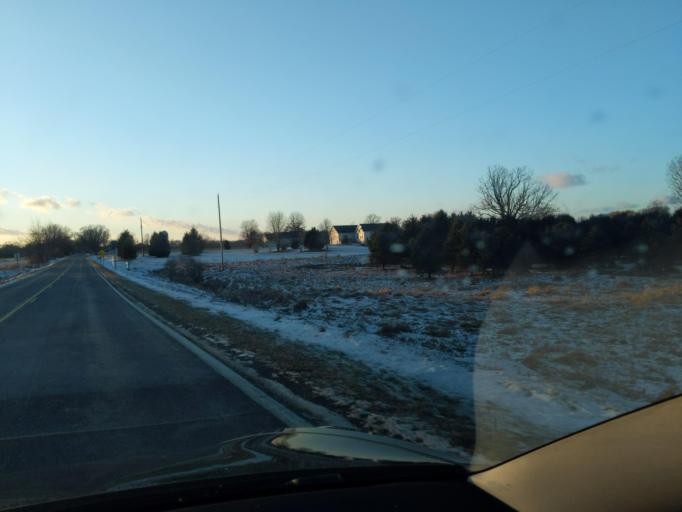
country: US
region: Michigan
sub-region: Ingham County
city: Stockbridge
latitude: 42.4467
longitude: -84.2212
